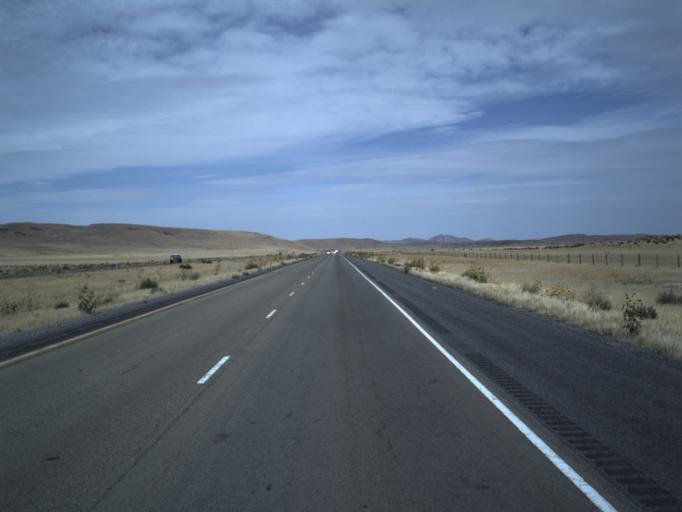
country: US
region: Utah
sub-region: Tooele County
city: Grantsville
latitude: 40.7928
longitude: -112.8358
